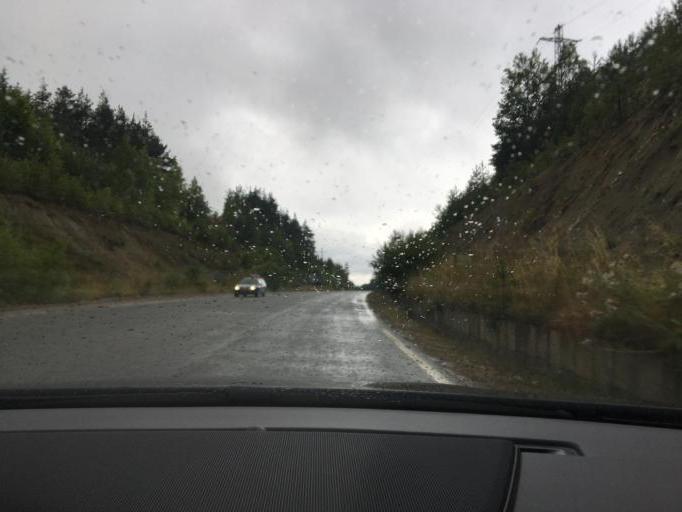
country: BG
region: Kyustendil
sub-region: Obshtina Kyustendil
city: Kyustendil
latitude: 42.2600
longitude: 22.5721
